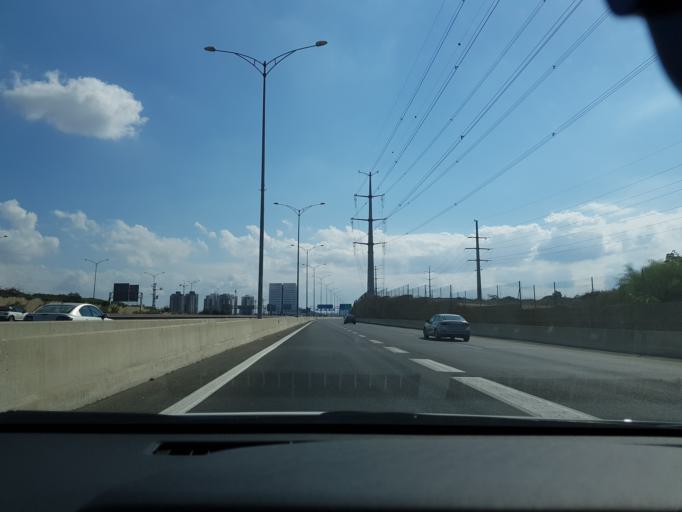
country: IL
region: Central District
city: Rishon LeZiyyon
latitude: 31.9516
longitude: 34.7902
